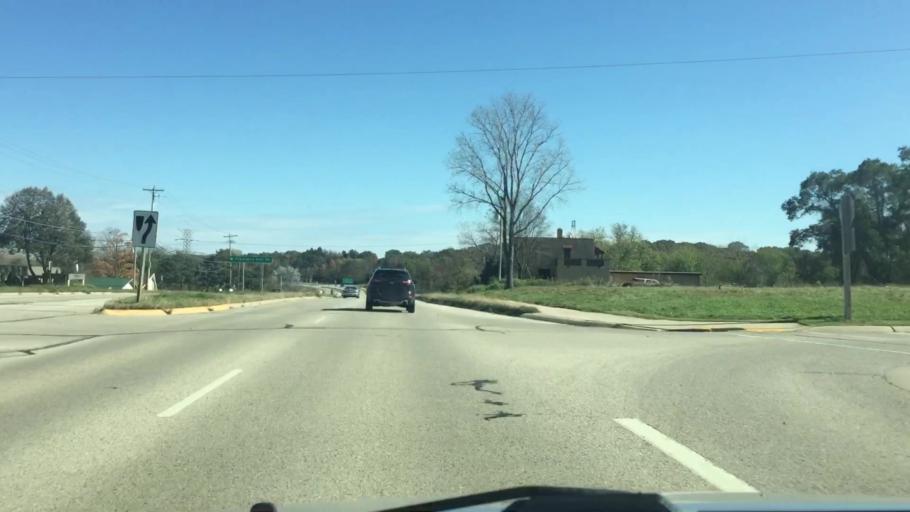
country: US
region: Wisconsin
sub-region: Waukesha County
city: Waukesha
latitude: 43.0137
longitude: -88.1812
